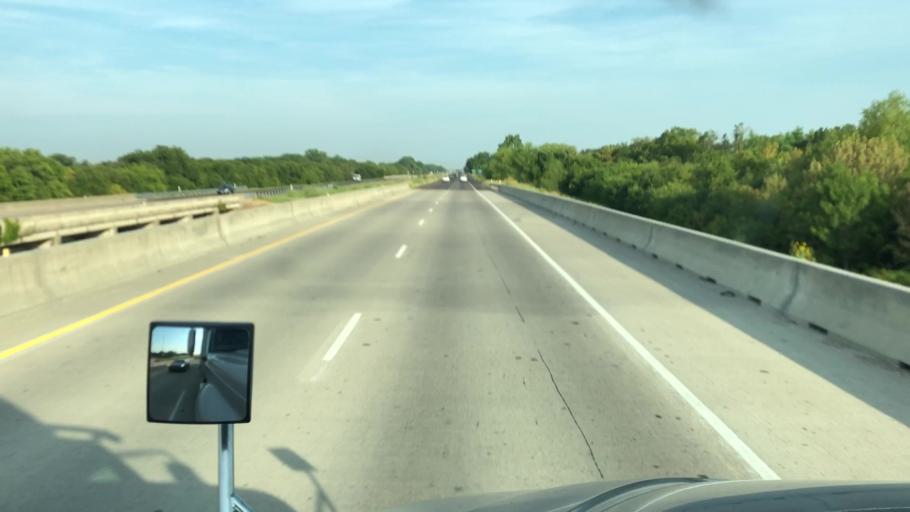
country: US
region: Texas
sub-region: McLennan County
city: Bellmead
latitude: 31.5347
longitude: -97.0275
